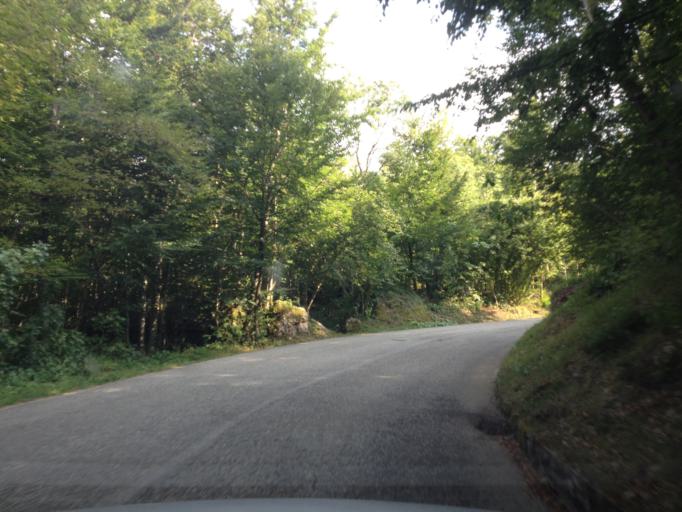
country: IT
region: Veneto
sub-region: Provincia di Vicenza
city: Laghi
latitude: 45.8186
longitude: 11.2756
